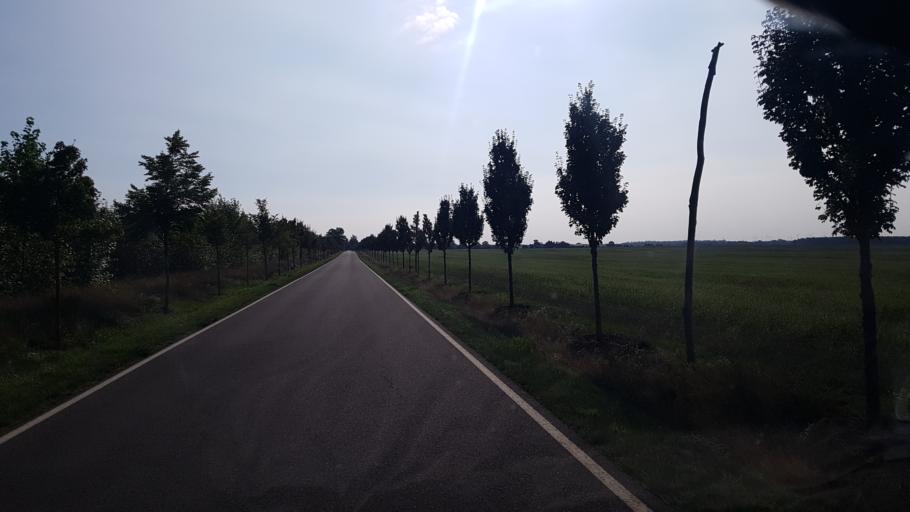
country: DE
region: Brandenburg
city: Luebben
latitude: 51.8829
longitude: 13.8281
